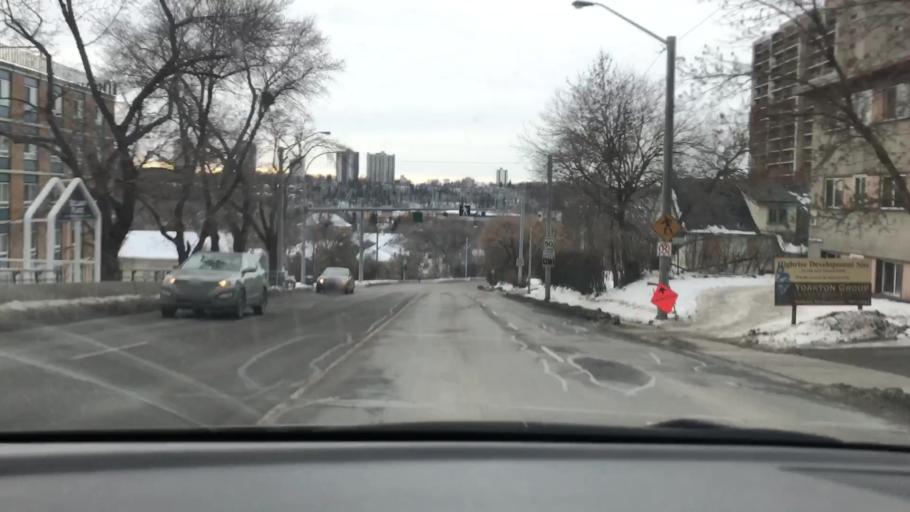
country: CA
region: Alberta
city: Edmonton
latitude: 53.5379
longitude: -113.4956
